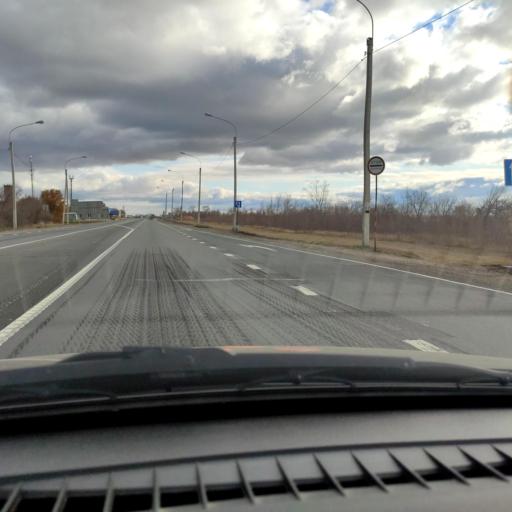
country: RU
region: Samara
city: Syzran'
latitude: 53.2098
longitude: 48.5091
